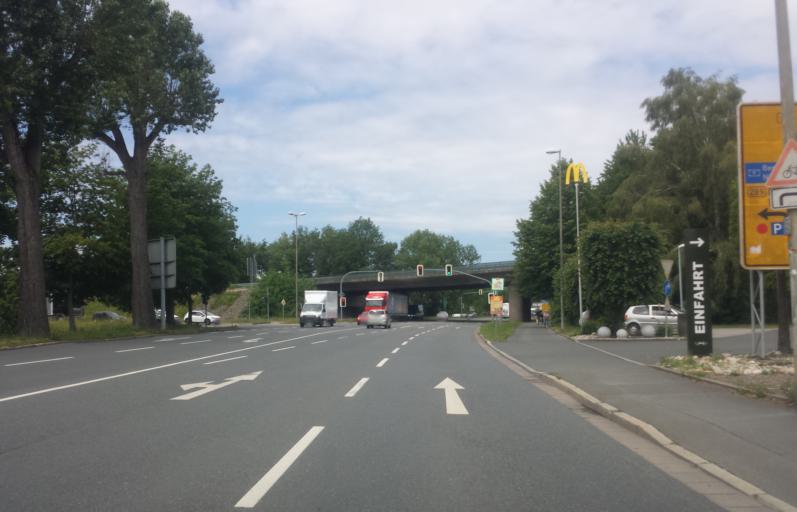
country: DE
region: Bavaria
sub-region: Upper Franconia
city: Kulmbach
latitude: 50.1130
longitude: 11.4463
